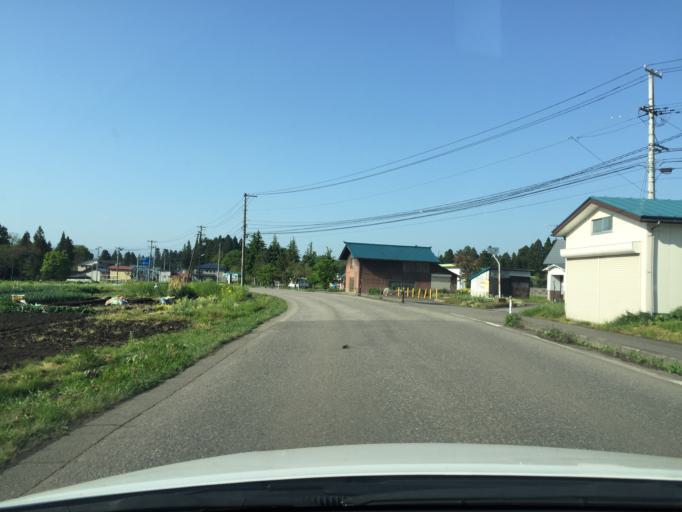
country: JP
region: Fukushima
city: Kitakata
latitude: 37.6507
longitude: 139.7744
